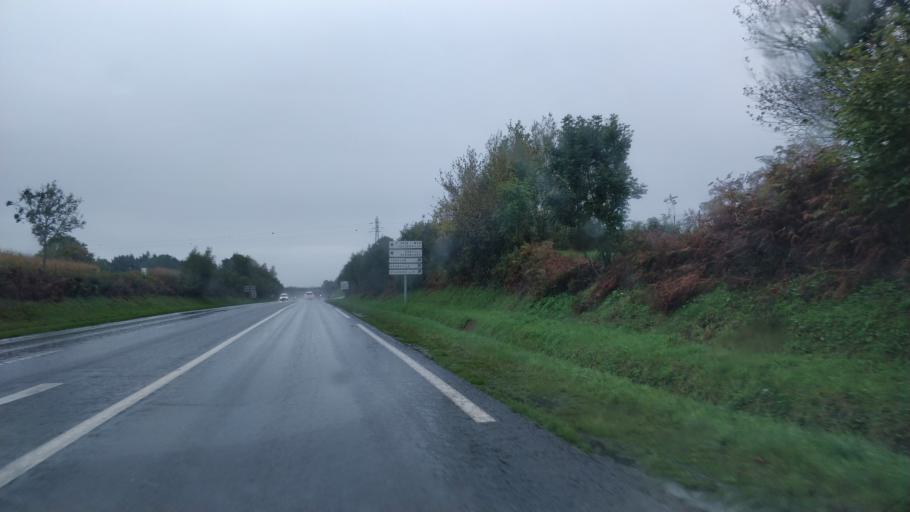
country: FR
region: Lower Normandy
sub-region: Departement de la Manche
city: Saint-Planchers
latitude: 48.8415
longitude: -1.5400
